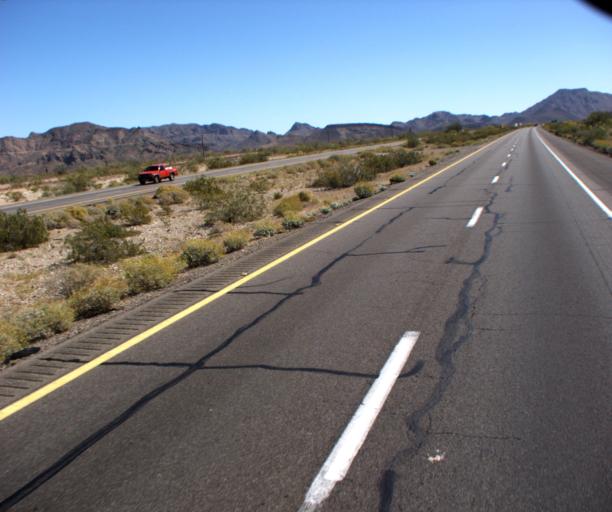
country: US
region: Arizona
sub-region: La Paz County
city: Quartzsite
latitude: 33.6777
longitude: -114.1127
